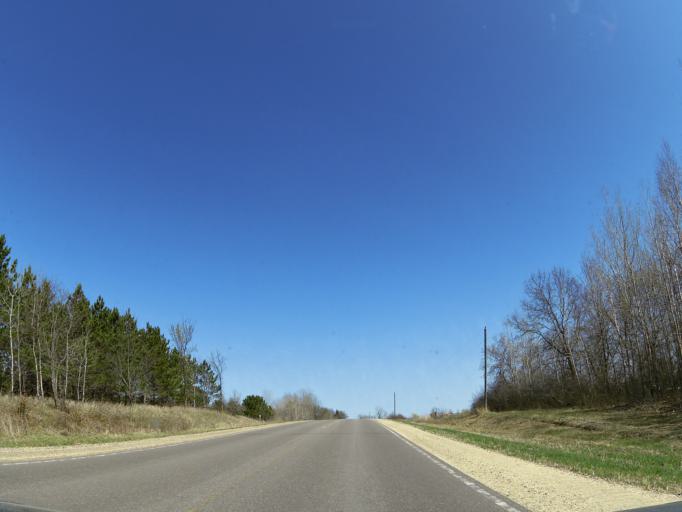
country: US
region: Wisconsin
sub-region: Saint Croix County
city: Hammond
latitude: 44.9343
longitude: -92.4416
